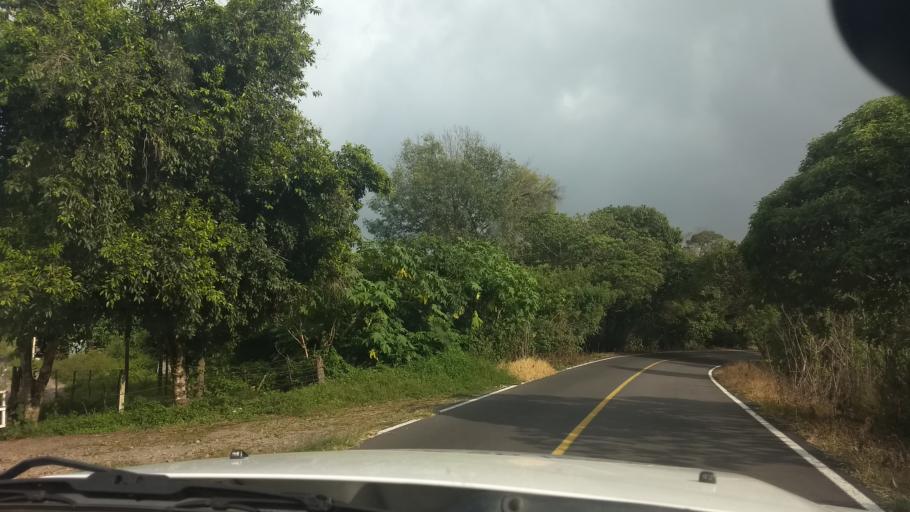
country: MX
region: Colima
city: Queseria
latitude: 19.4040
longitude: -103.6176
